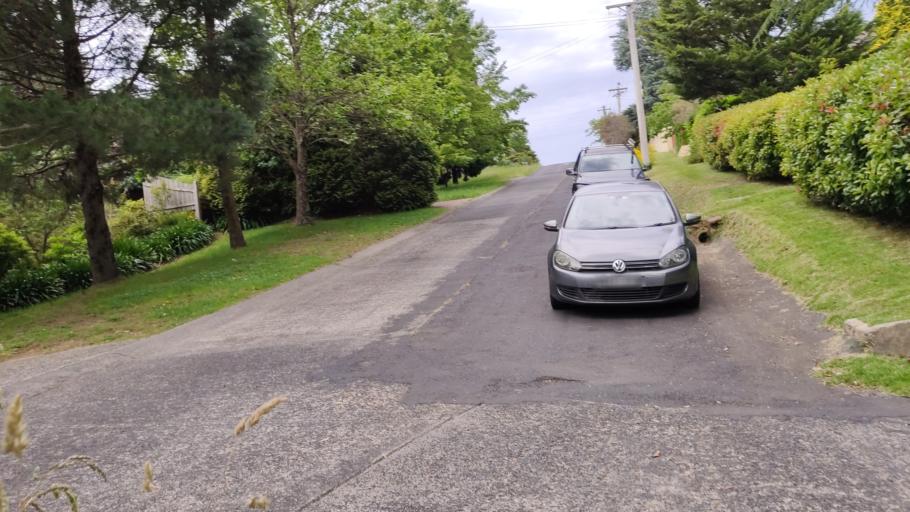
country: AU
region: New South Wales
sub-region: Blue Mountains Municipality
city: Leura
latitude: -33.7154
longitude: 150.3276
